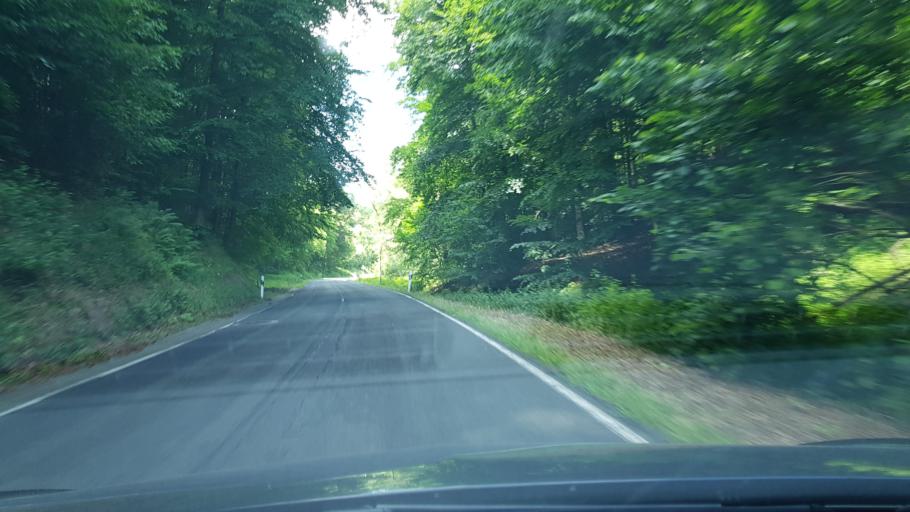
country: DE
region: Rheinland-Pfalz
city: Langenfeld
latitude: 50.3776
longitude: 7.1050
